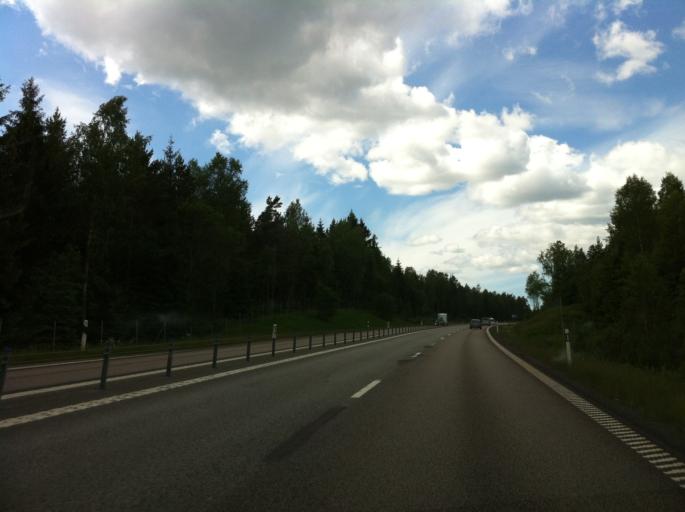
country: SE
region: Vaestra Goetaland
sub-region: Amals Kommun
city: Amal
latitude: 59.1003
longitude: 12.7806
